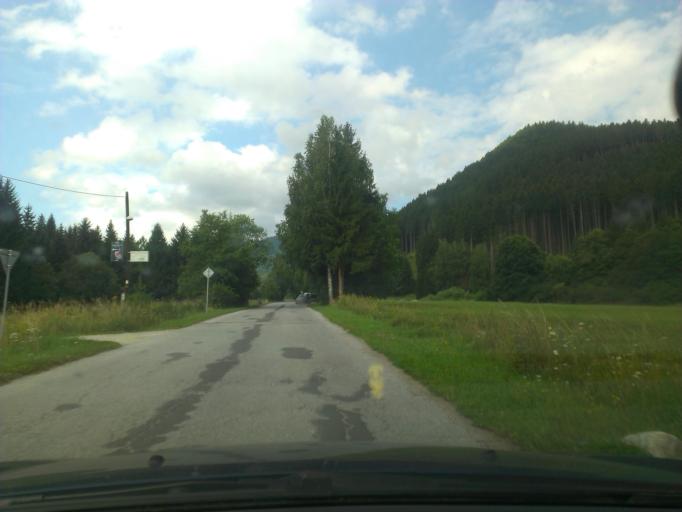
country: SK
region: Zilinsky
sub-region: Okres Zilina
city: Vrutky
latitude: 49.1067
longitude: 18.8951
